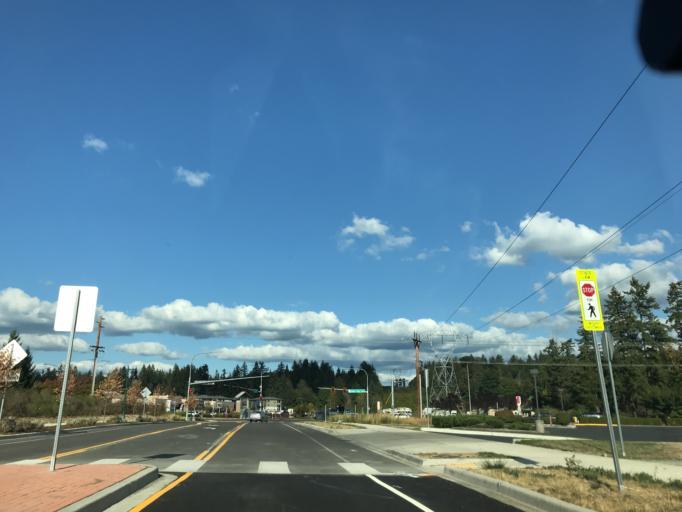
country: US
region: Washington
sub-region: King County
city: Ravensdale
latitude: 47.3580
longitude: -122.0217
